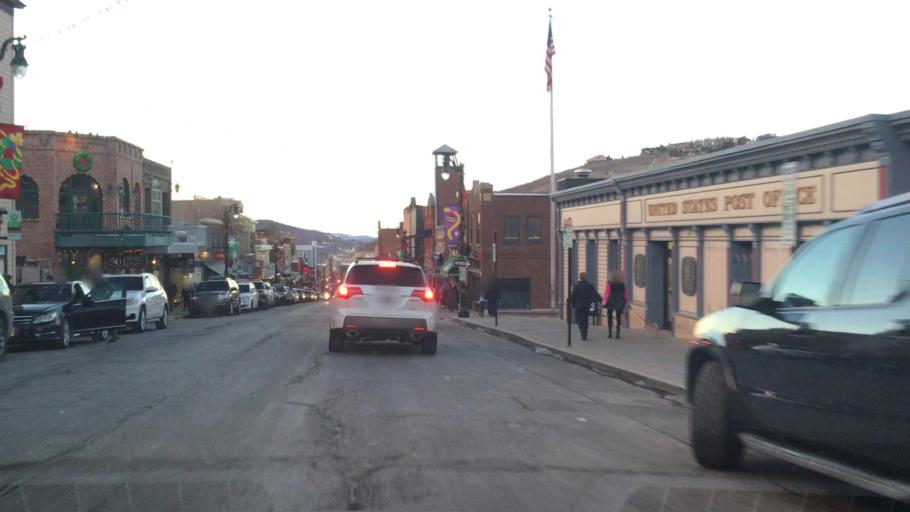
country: US
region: Utah
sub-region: Summit County
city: Park City
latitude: 40.6439
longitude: -111.4959
